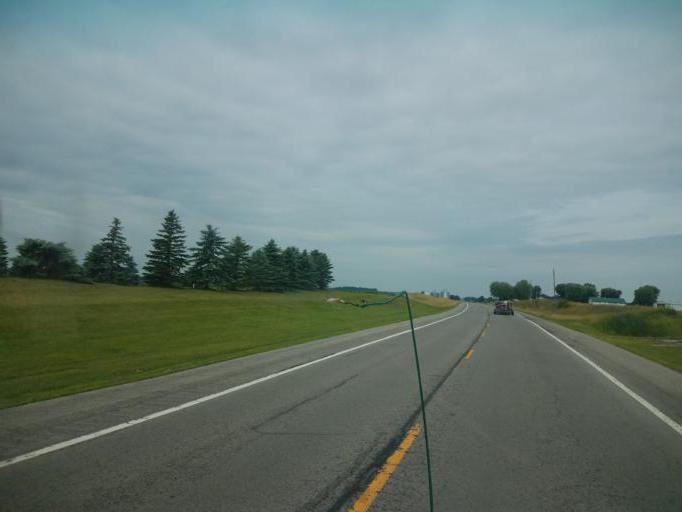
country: US
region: Ohio
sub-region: Hardin County
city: Kenton
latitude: 40.6902
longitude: -83.6930
